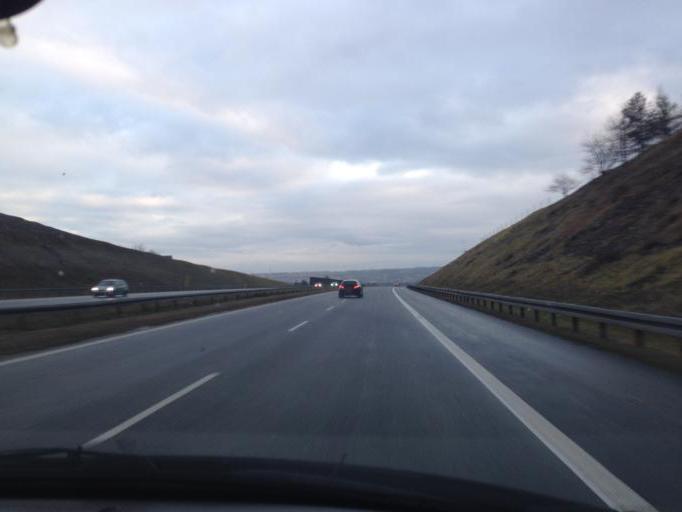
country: PL
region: Lesser Poland Voivodeship
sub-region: Powiat chrzanowski
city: Grojec
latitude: 50.0976
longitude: 19.5599
